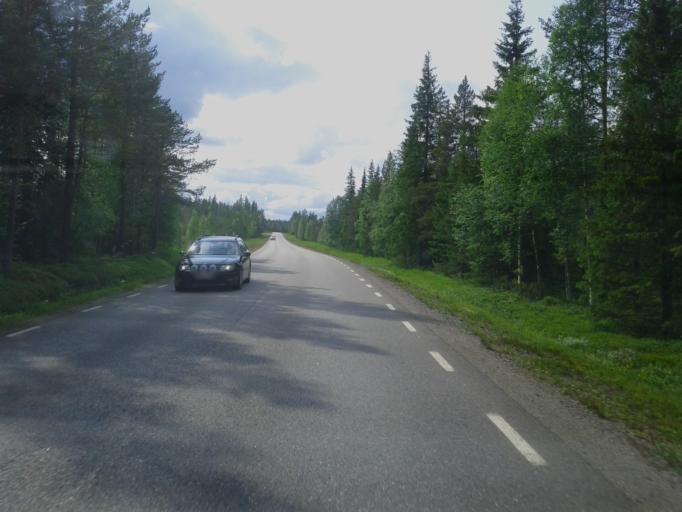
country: SE
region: Vaesterbotten
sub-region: Mala Kommun
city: Mala
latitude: 65.2319
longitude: 18.5628
